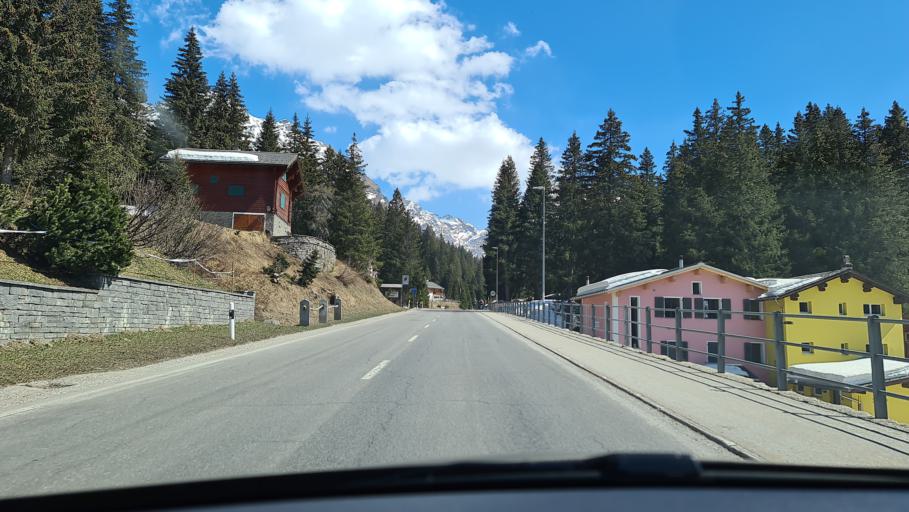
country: CH
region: Grisons
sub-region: Hinterrhein District
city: Hinterrhein
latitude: 46.4584
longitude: 9.1941
